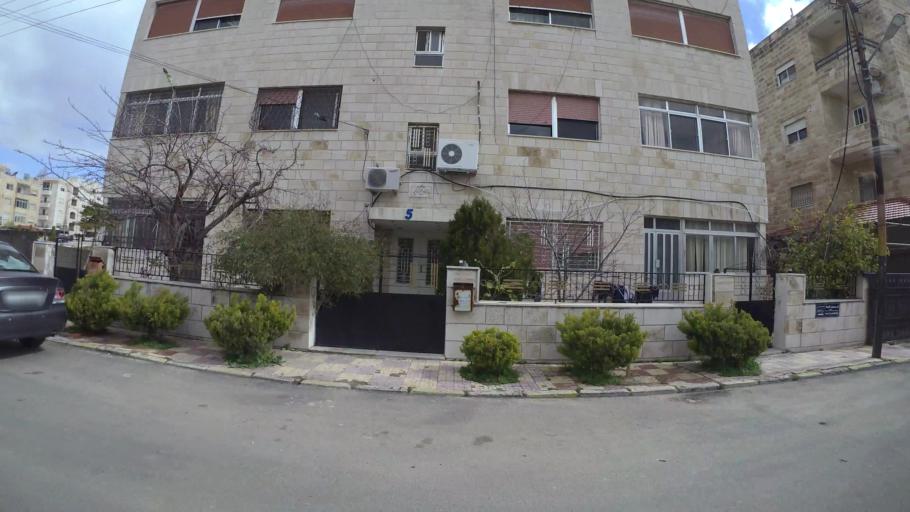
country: JO
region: Amman
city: Wadi as Sir
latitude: 31.9467
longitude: 35.8433
